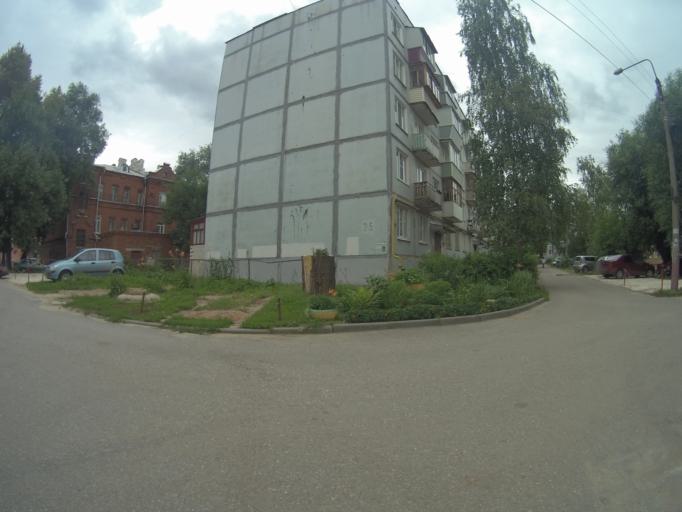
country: RU
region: Vladimir
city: Vladimir
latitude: 56.1286
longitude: 40.3716
